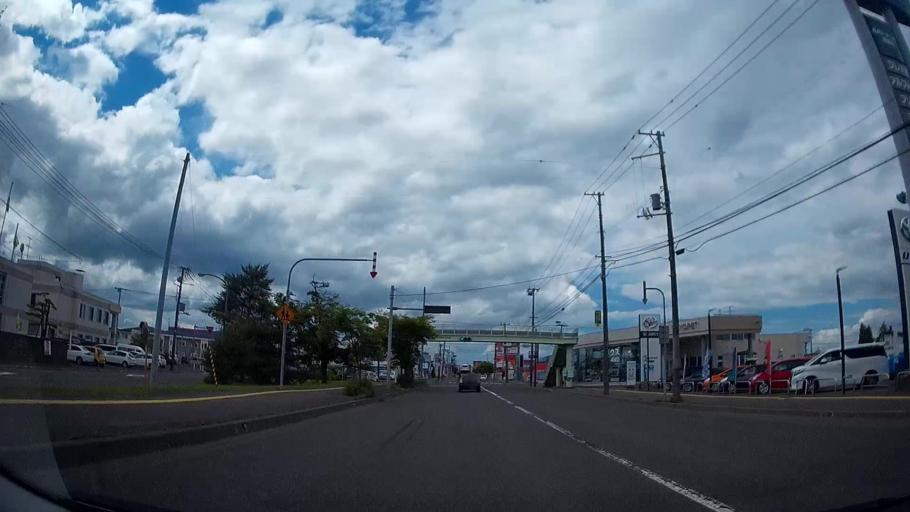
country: JP
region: Hokkaido
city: Chitose
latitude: 42.8726
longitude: 141.5855
